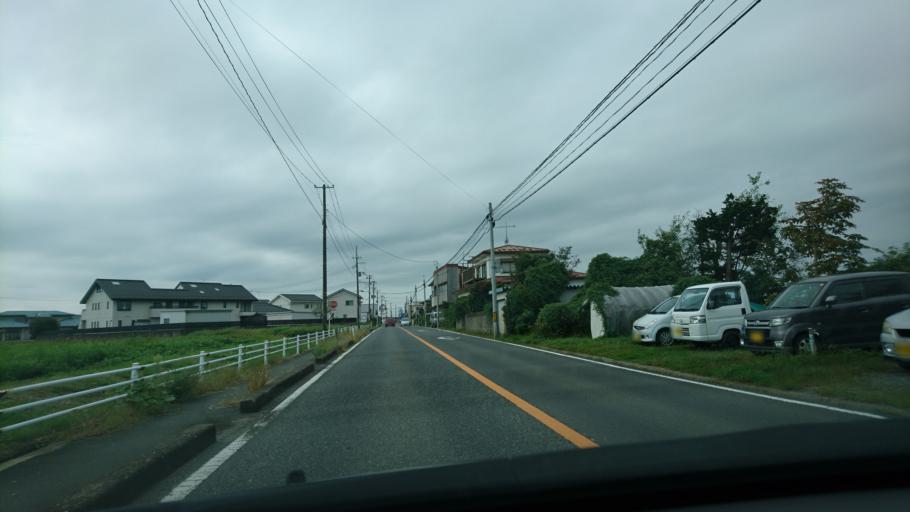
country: JP
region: Iwate
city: Ichinoseki
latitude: 38.7512
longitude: 141.0569
